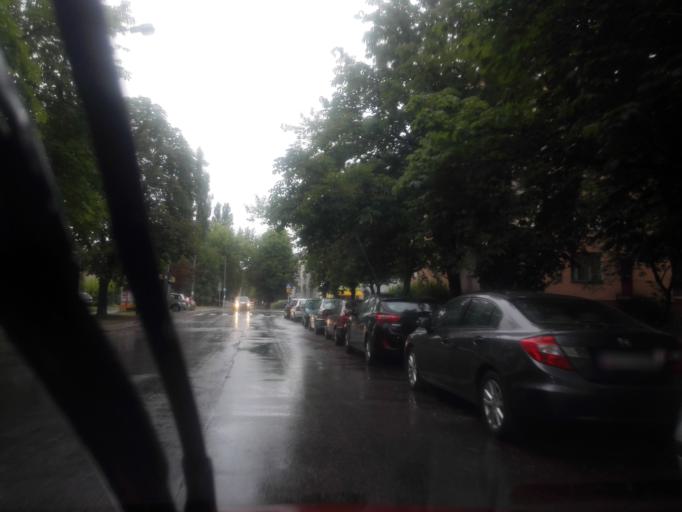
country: PL
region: Masovian Voivodeship
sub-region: Warszawa
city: Mokotow
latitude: 52.1918
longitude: 21.0109
